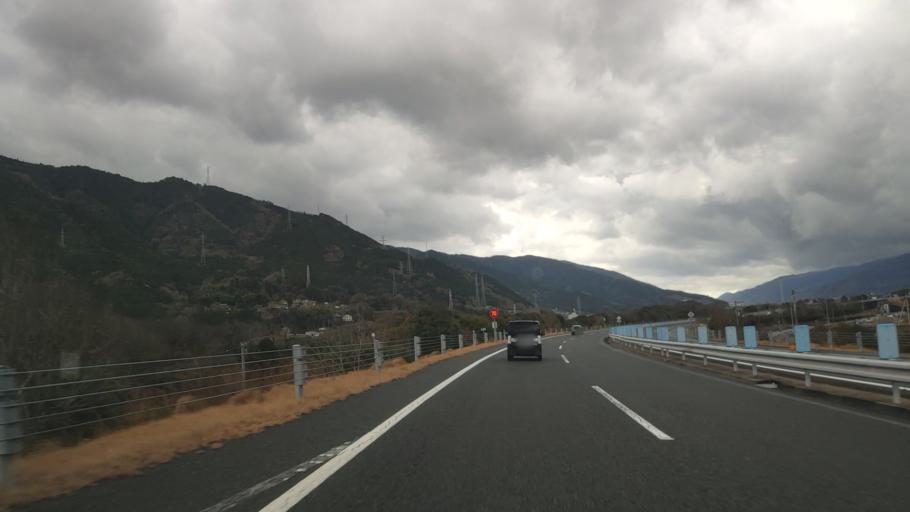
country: JP
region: Tokushima
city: Ikedacho
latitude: 34.0373
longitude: 133.9044
